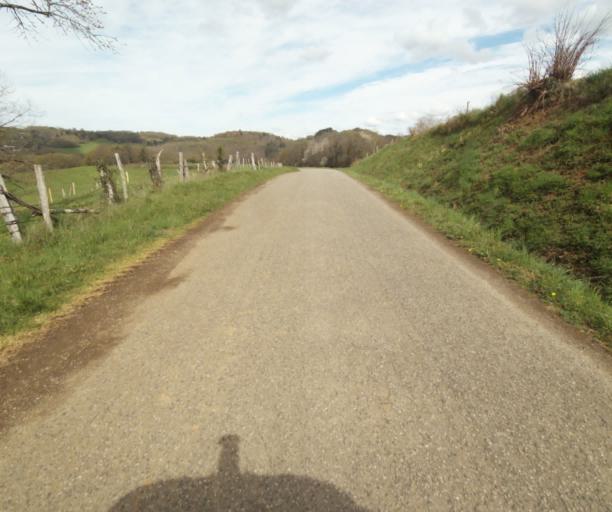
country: FR
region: Limousin
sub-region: Departement de la Correze
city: Laguenne
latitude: 45.2493
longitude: 1.8328
